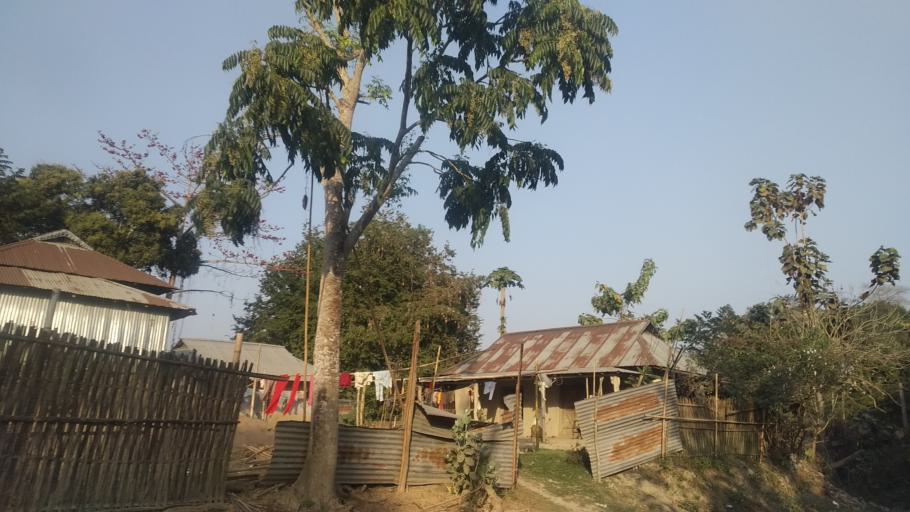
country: IN
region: Tripura
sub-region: West Tripura
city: Sonamura
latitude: 23.4404
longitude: 91.3622
